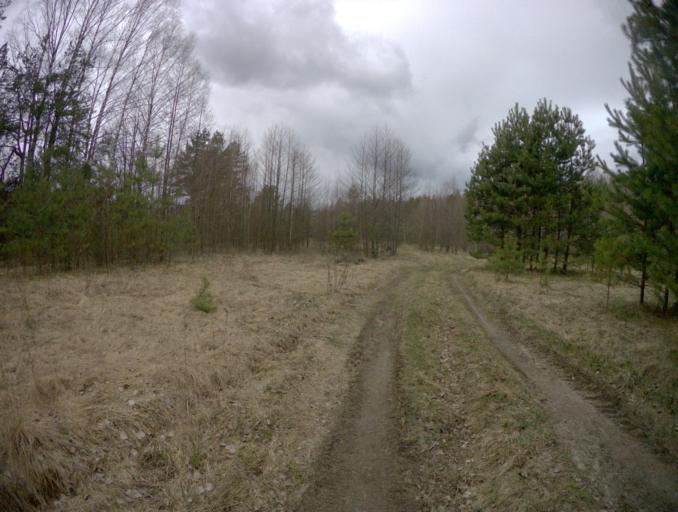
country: RU
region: Vladimir
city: Sudogda
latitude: 56.0466
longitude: 40.7924
